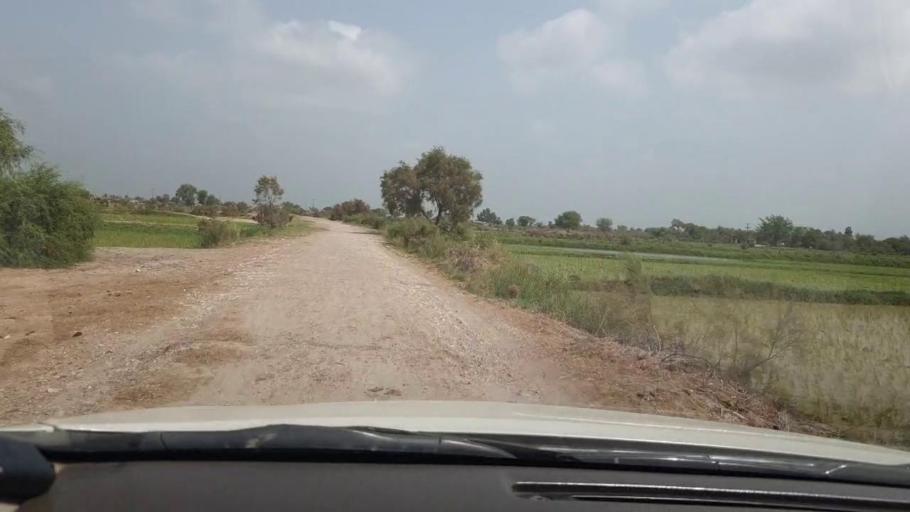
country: PK
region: Sindh
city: Garhi Yasin
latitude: 28.0161
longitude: 68.5286
